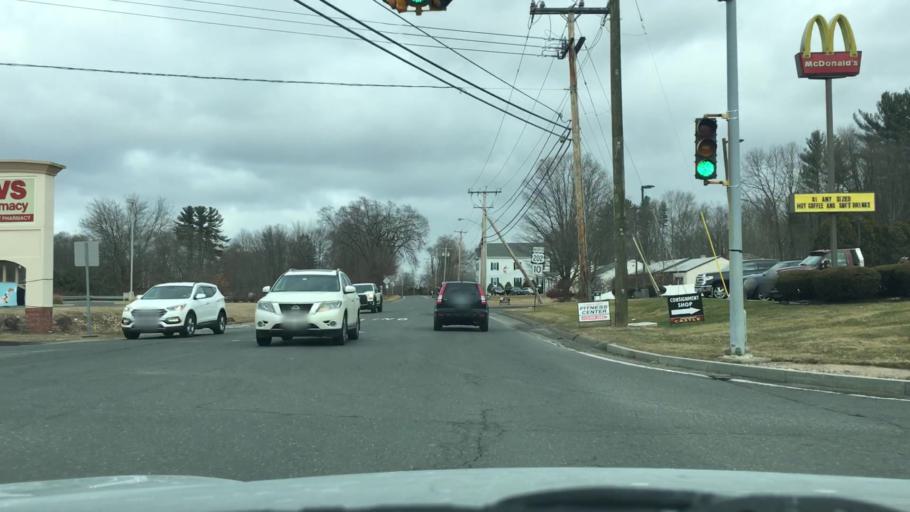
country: US
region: Massachusetts
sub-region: Hampden County
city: Southwick
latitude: 42.0255
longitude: -72.7862
